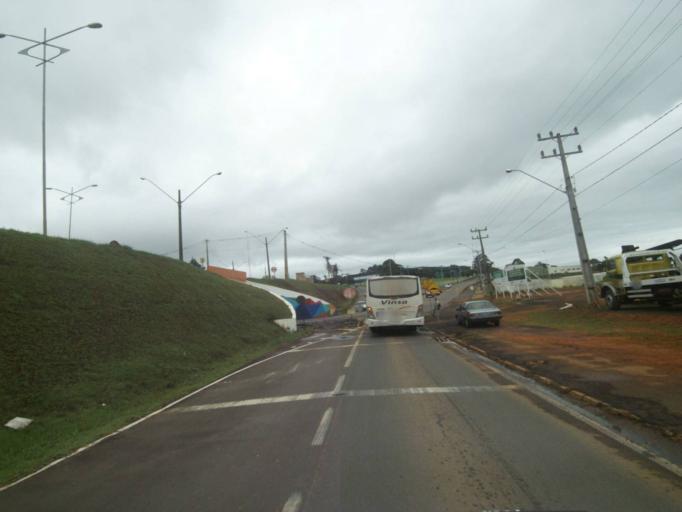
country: BR
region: Parana
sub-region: Telemaco Borba
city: Telemaco Borba
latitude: -24.3339
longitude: -50.6522
